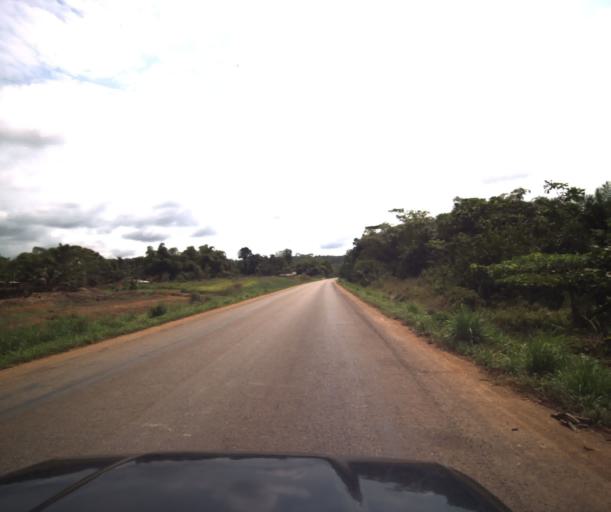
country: CM
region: Centre
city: Eseka
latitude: 3.8572
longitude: 10.5413
